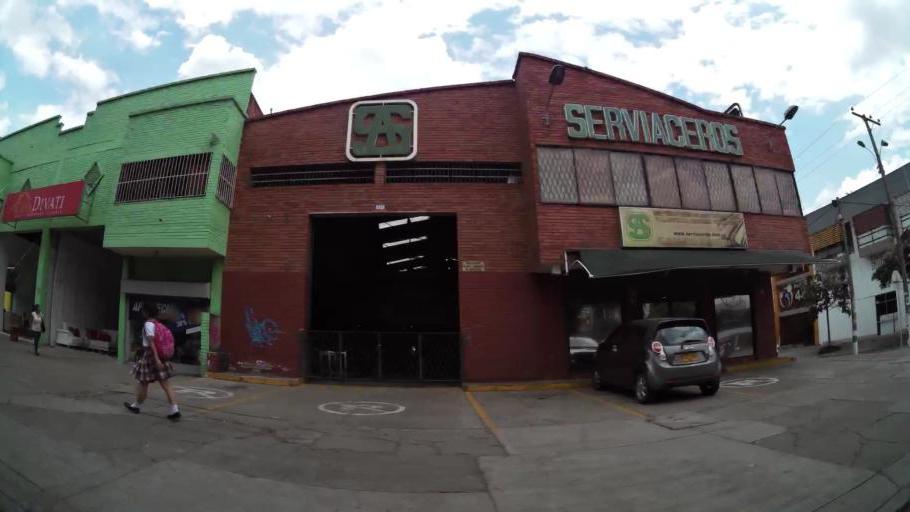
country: CO
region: Valle del Cauca
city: Cali
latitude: 3.4679
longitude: -76.5089
